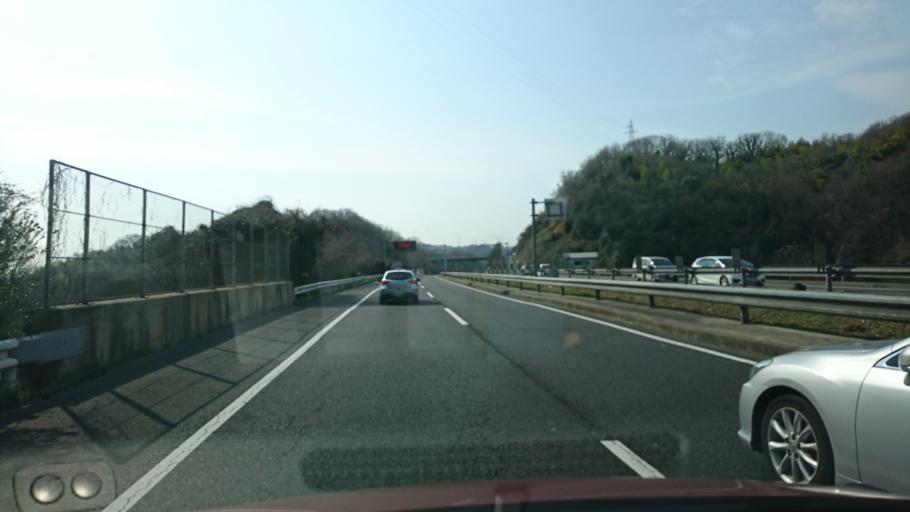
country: JP
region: Hiroshima
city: Onomichi
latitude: 34.4393
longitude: 133.2260
